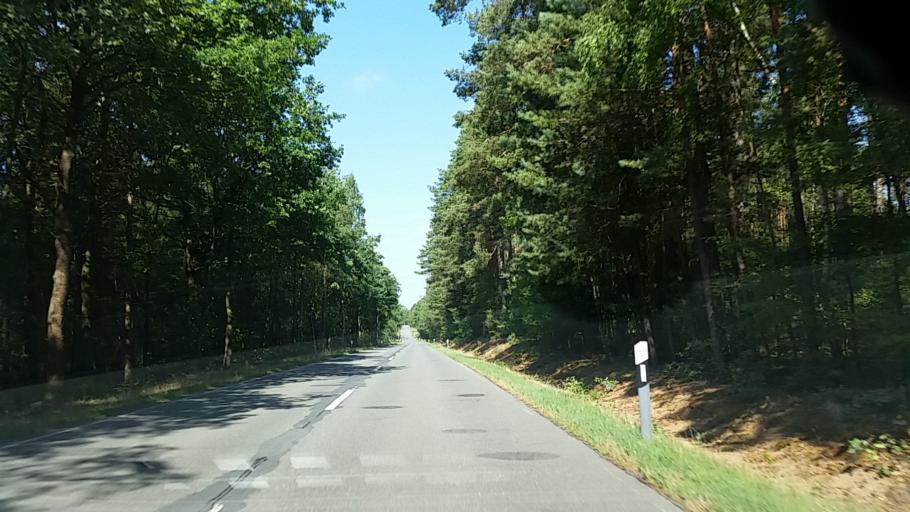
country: DE
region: Lower Saxony
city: Jelmstorf
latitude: 53.1209
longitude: 10.5391
